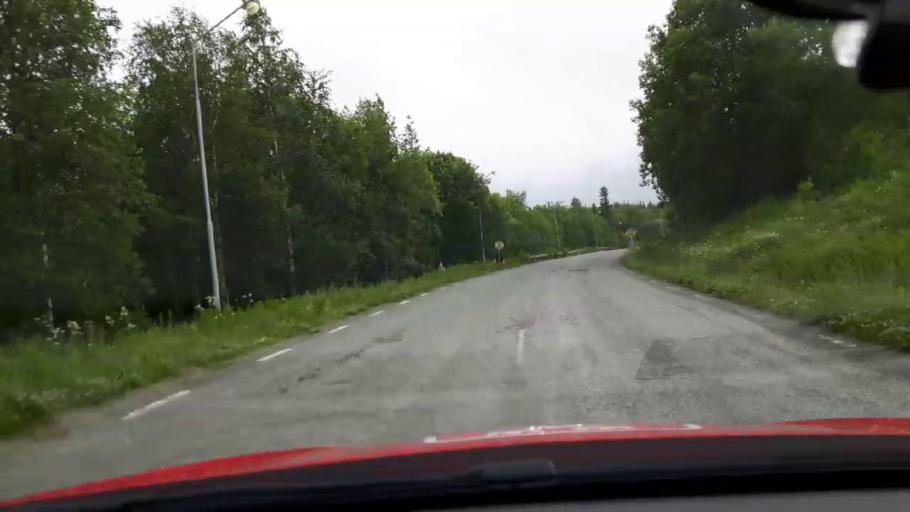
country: SE
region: Jaemtland
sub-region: Are Kommun
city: Are
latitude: 63.2544
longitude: 12.4539
